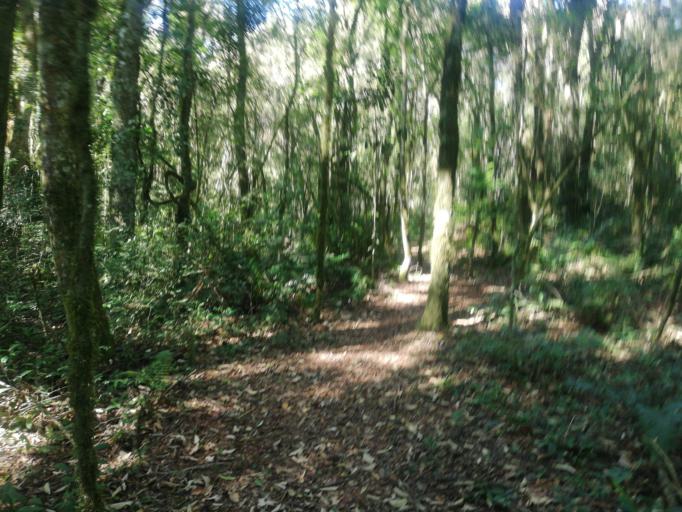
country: AR
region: Misiones
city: Colonia Wanda
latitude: -25.8594
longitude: -54.1685
